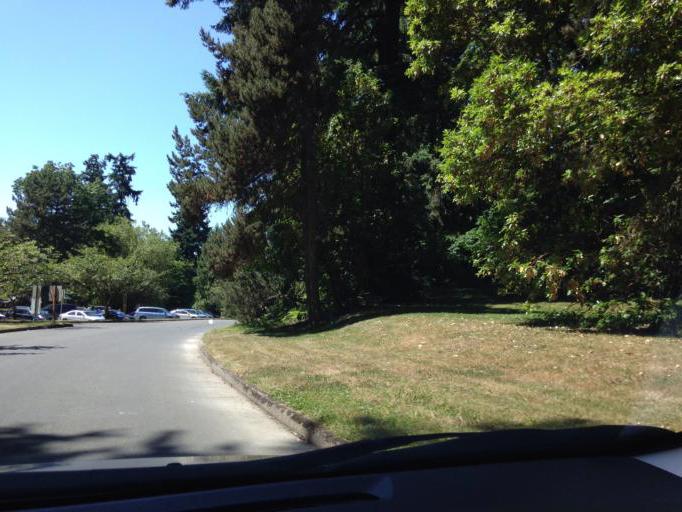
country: US
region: Washington
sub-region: King County
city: Mercer Island
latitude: 47.5513
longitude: -122.2532
